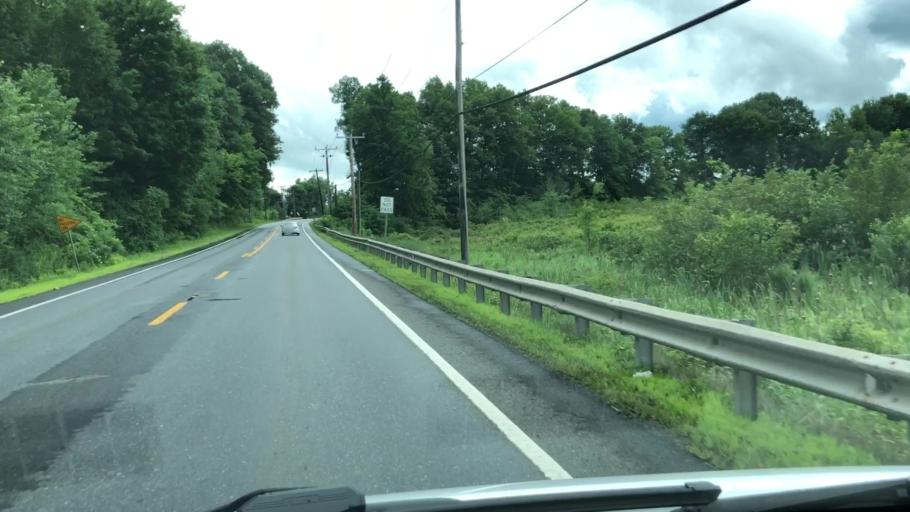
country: US
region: Massachusetts
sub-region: Franklin County
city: South Deerfield
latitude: 42.5314
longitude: -72.6040
